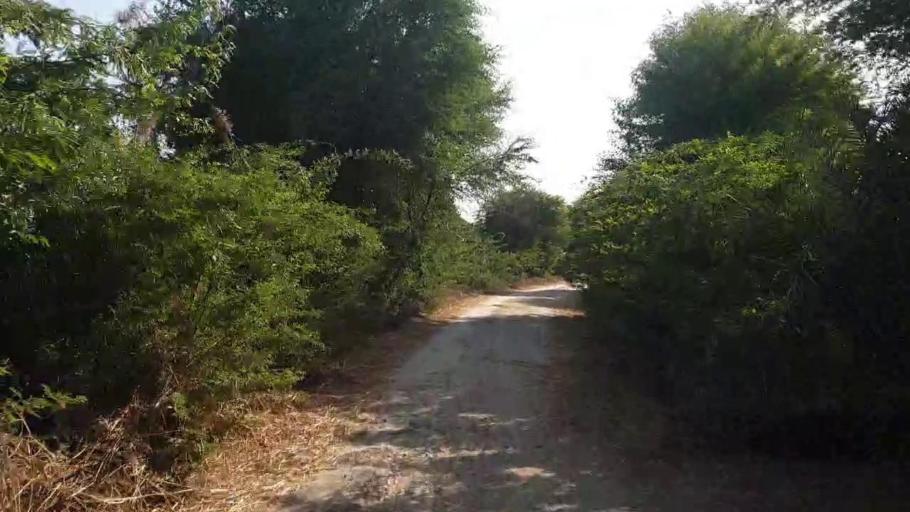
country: PK
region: Sindh
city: Matli
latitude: 25.0120
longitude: 68.7402
